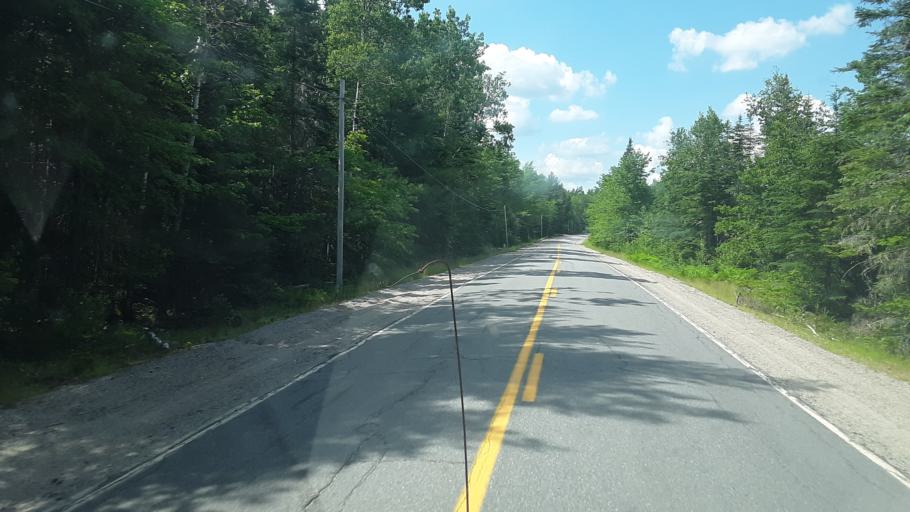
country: US
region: Maine
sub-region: Washington County
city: Machias
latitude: 44.8783
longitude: -67.6205
